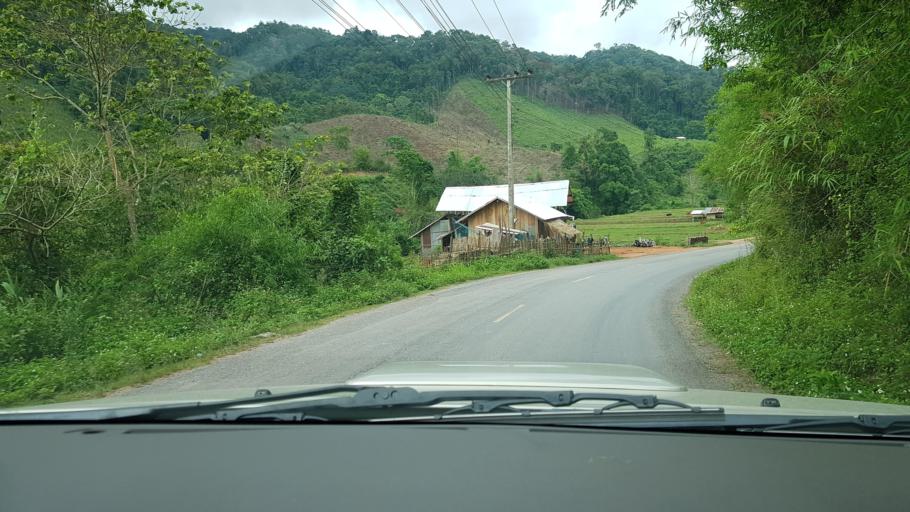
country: LA
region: Oudomxai
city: Muang Xay
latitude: 20.5554
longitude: 101.9120
